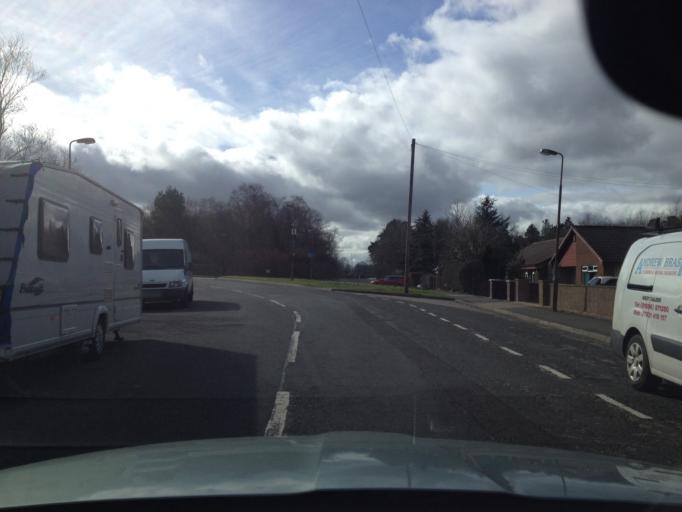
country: GB
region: Scotland
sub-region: West Lothian
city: Livingston
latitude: 55.8685
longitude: -3.5302
